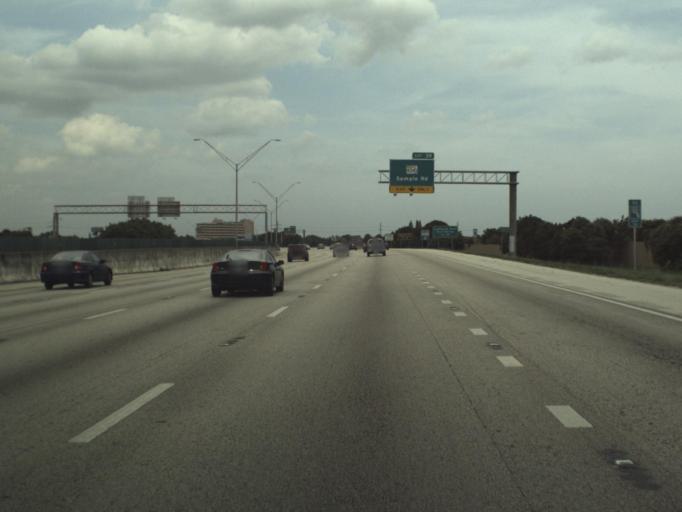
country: US
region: Florida
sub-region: Broward County
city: Kendall Green
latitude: 26.2662
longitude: -80.1280
